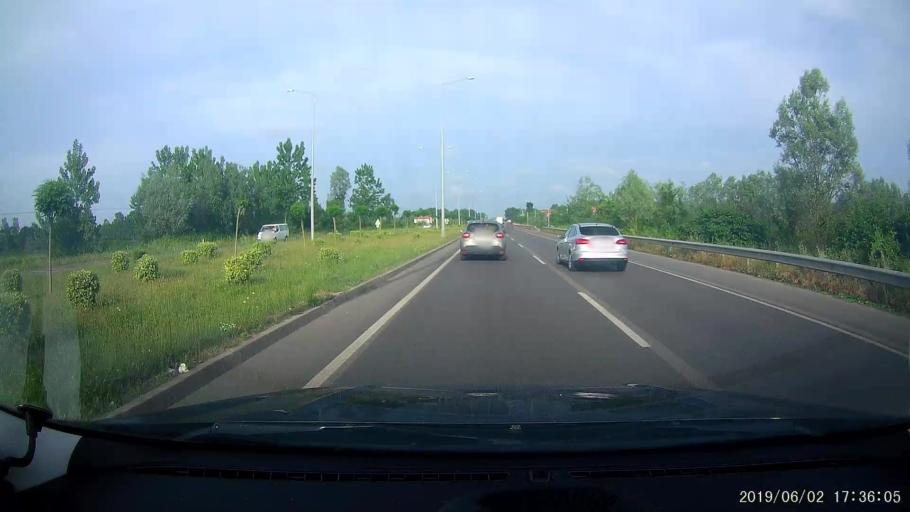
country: TR
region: Samsun
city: Terme
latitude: 41.2191
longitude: 36.8928
